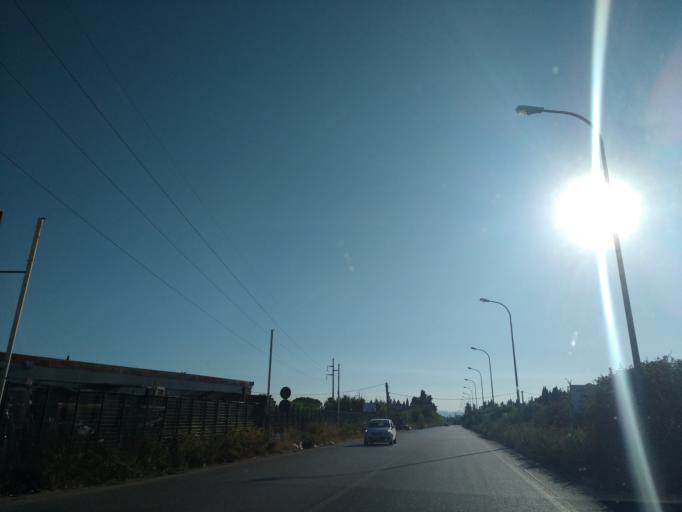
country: IT
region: Sicily
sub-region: Provincia di Siracusa
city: Siracusa
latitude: 37.0666
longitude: 15.2602
